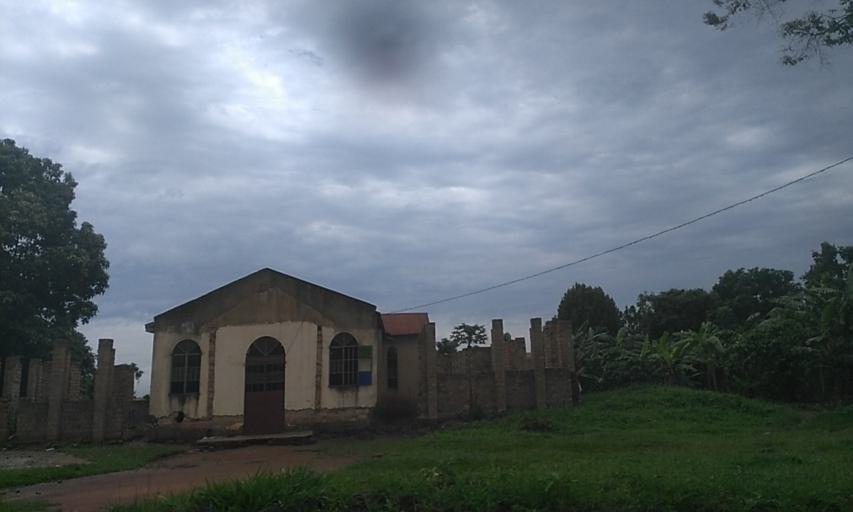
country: UG
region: Central Region
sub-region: Wakiso District
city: Bweyogerere
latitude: 0.3959
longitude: 32.6823
